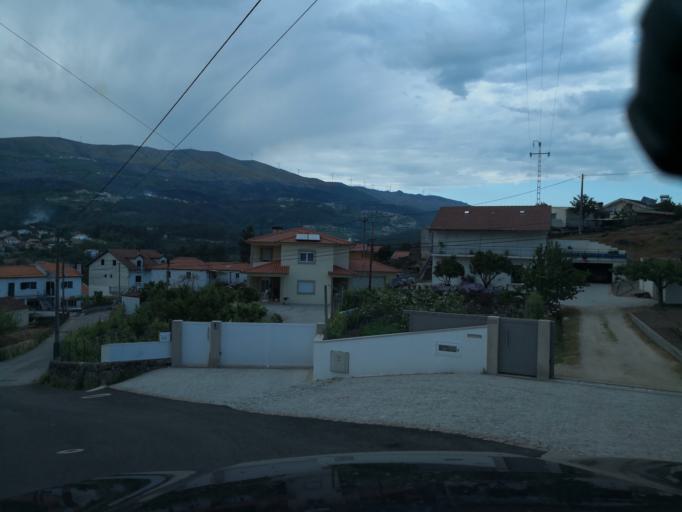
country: PT
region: Vila Real
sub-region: Vila Real
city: Vila Real
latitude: 41.3226
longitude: -7.7334
